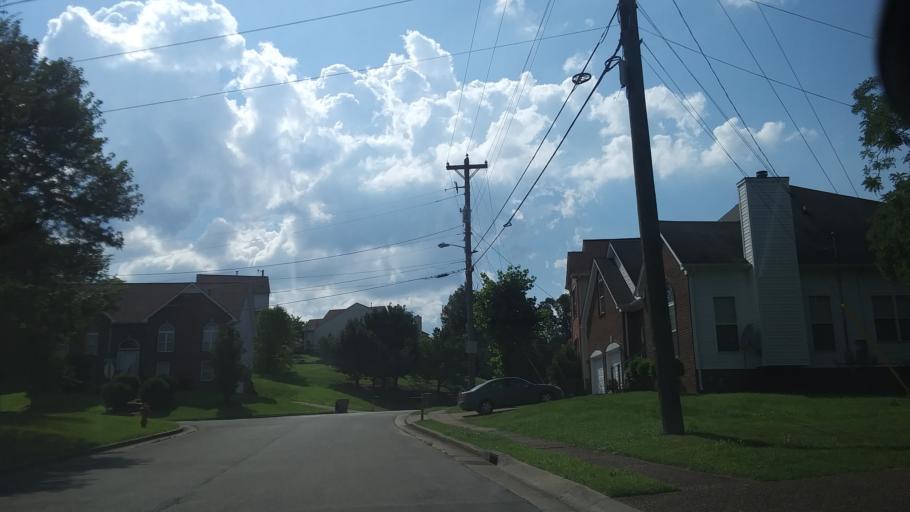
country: US
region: Tennessee
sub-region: Rutherford County
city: La Vergne
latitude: 36.0945
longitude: -86.6280
